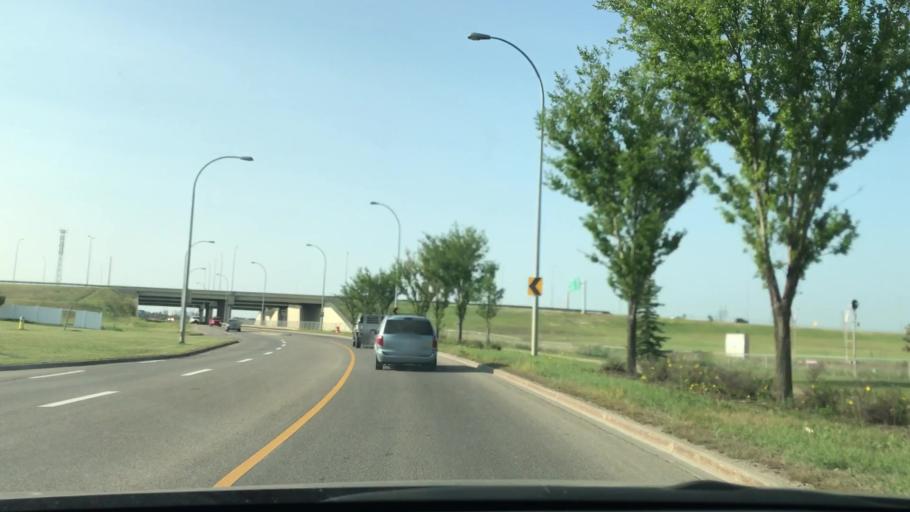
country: CA
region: Alberta
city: Edmonton
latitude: 53.4404
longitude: -113.4845
